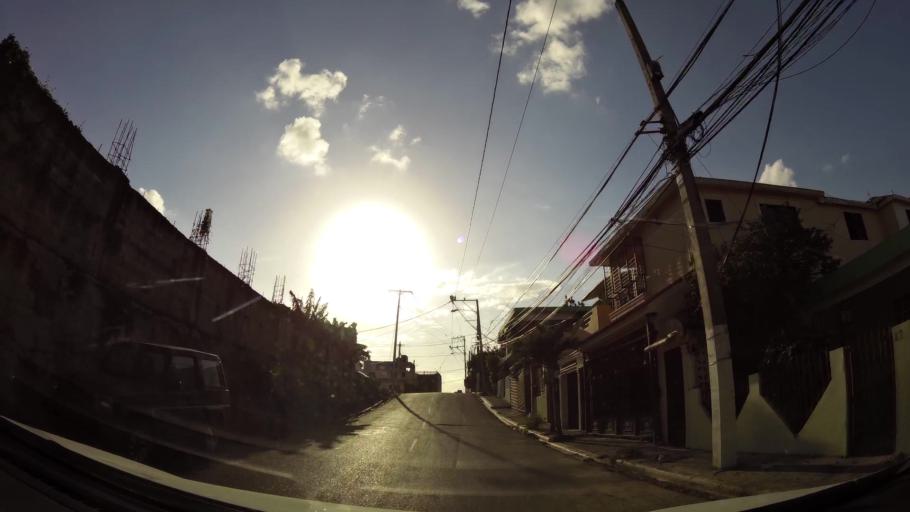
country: DO
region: Nacional
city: Ensanche Luperon
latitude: 18.5440
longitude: -69.9022
